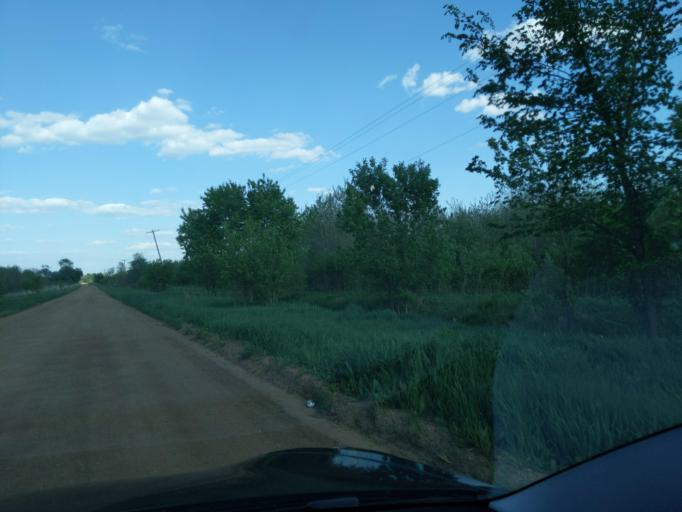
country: US
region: Michigan
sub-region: Eaton County
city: Potterville
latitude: 42.6828
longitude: -84.7359
